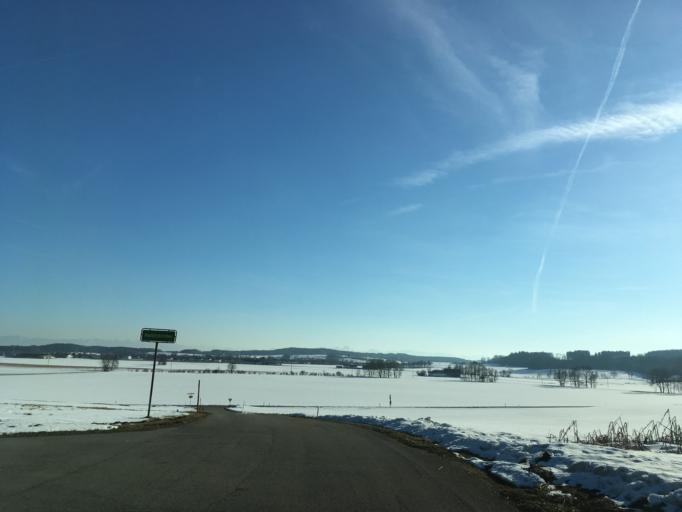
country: DE
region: Bavaria
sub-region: Upper Bavaria
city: Steinhoring
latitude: 48.1044
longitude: 12.0258
